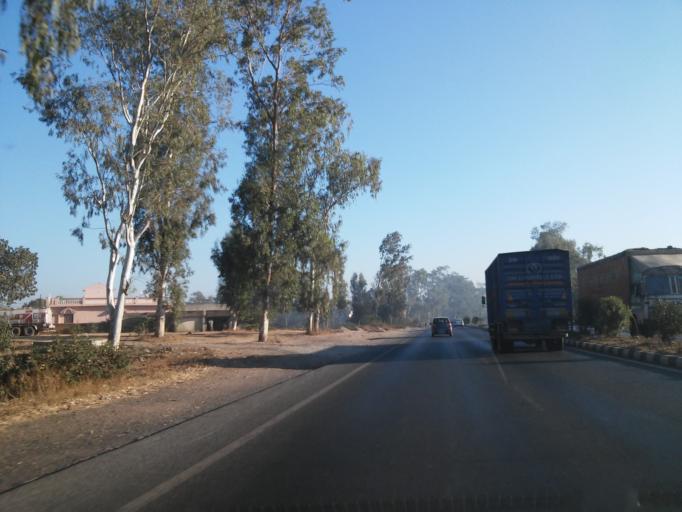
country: IN
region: Rajasthan
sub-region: Dungarpur
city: Dungarpur
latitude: 23.9127
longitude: 73.5564
